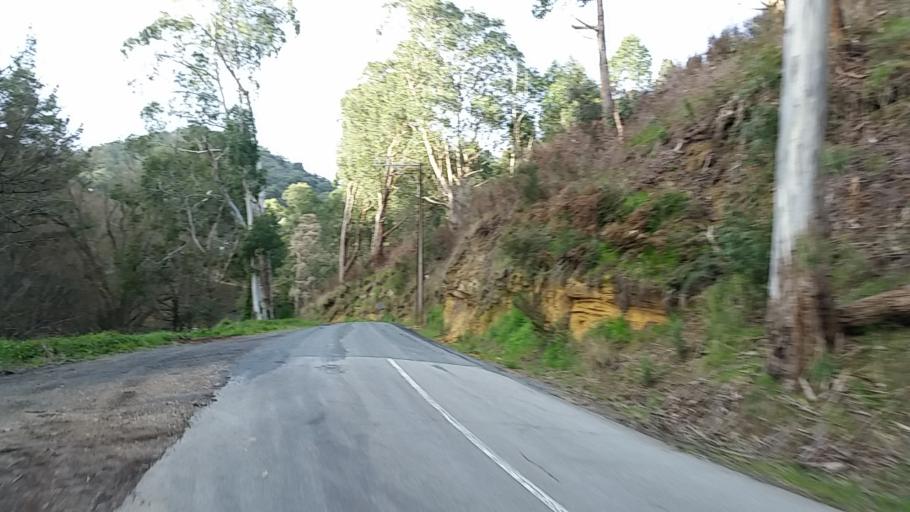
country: AU
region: South Australia
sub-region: Adelaide Hills
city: Adelaide Hills
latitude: -34.9274
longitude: 138.7689
